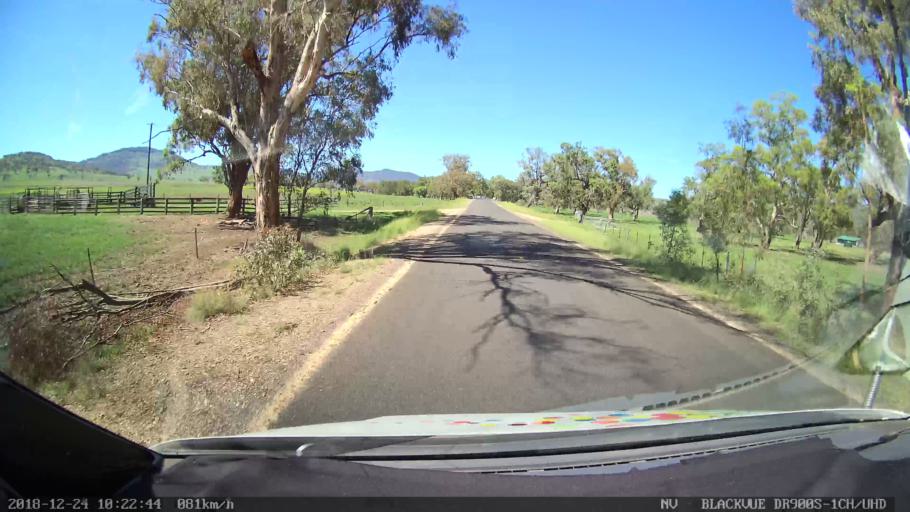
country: AU
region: New South Wales
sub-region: Liverpool Plains
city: Quirindi
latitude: -31.7678
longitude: 150.5425
